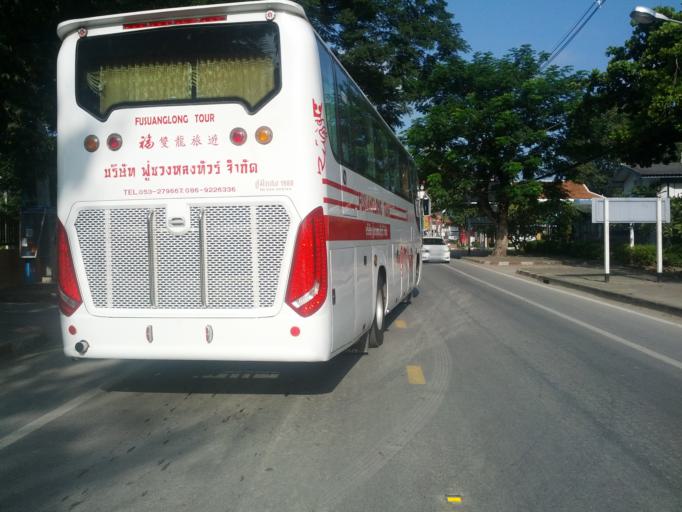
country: TH
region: Chiang Mai
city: San Kamphaeng
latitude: 18.7673
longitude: 99.0753
